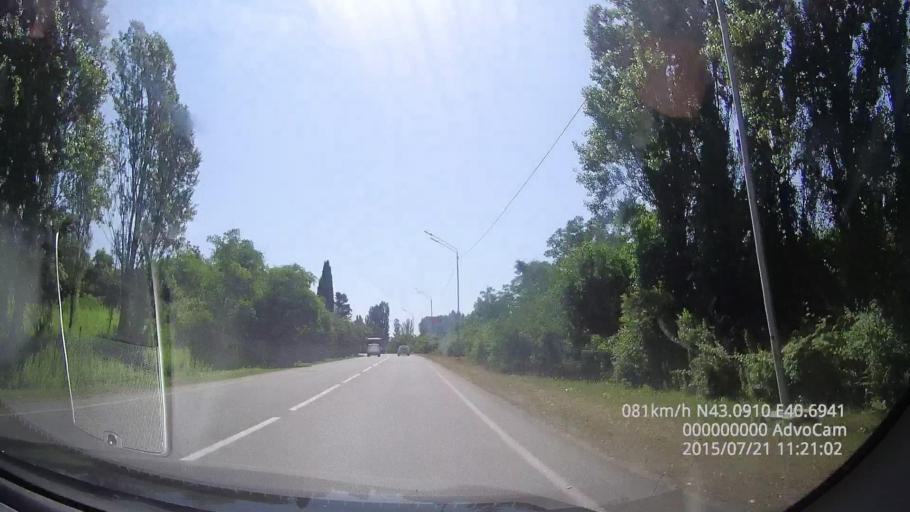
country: GE
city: P'rimorsk'oe
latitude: 43.0908
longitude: 40.6944
